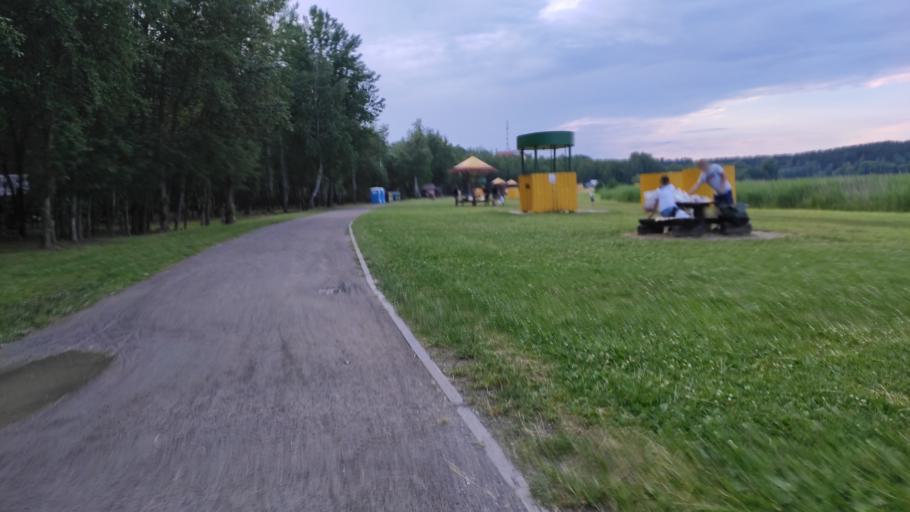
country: BY
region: Minsk
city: Zhdanovichy
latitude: 53.9568
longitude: 27.4463
